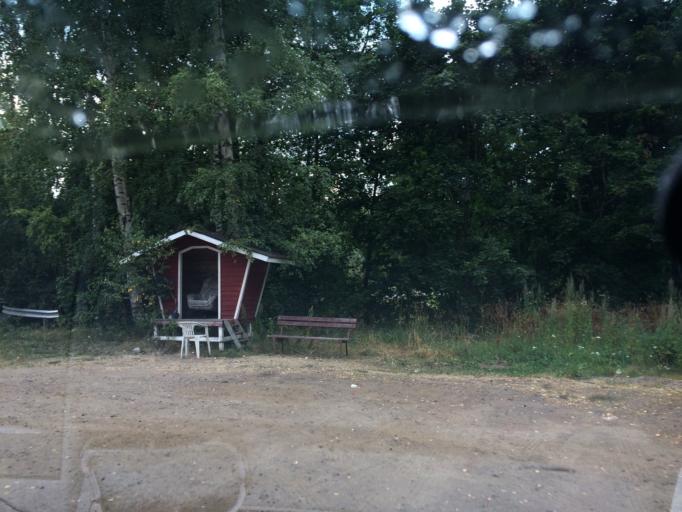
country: FI
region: Pirkanmaa
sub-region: Tampere
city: Luopioinen
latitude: 61.2763
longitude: 24.6672
